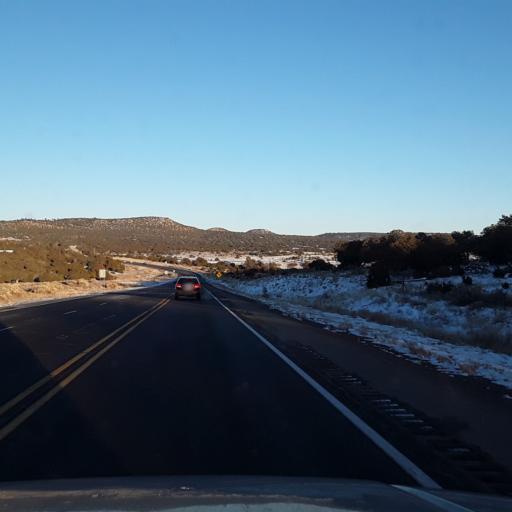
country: US
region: New Mexico
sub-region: Lincoln County
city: Carrizozo
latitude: 34.2388
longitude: -105.6038
